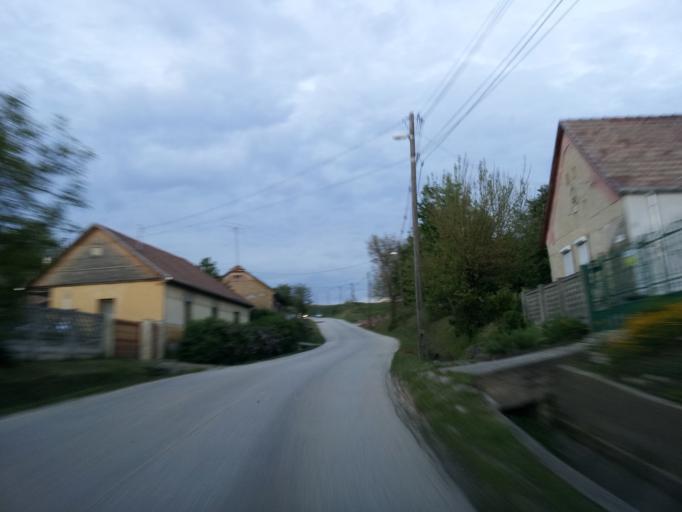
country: HU
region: Komarom-Esztergom
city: Csolnok
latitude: 47.6690
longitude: 18.7209
